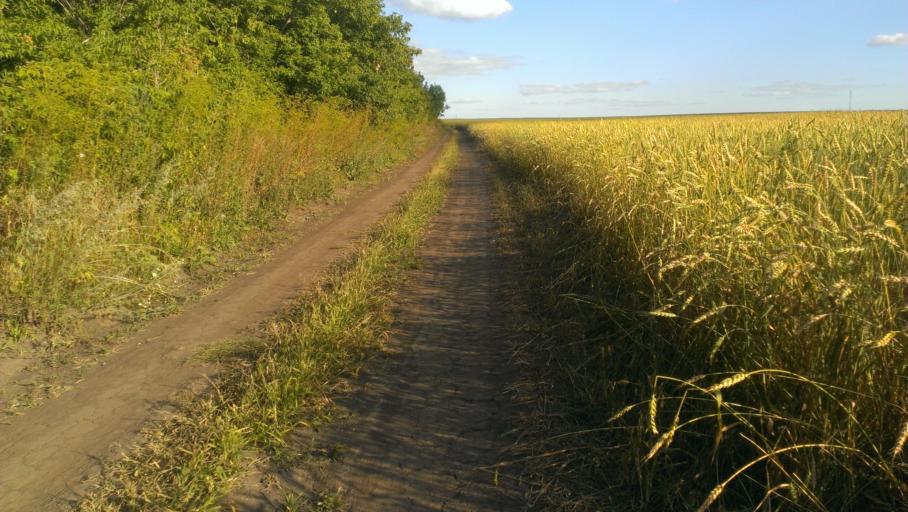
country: RU
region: Altai Krai
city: Gon'ba
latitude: 53.3862
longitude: 83.6017
